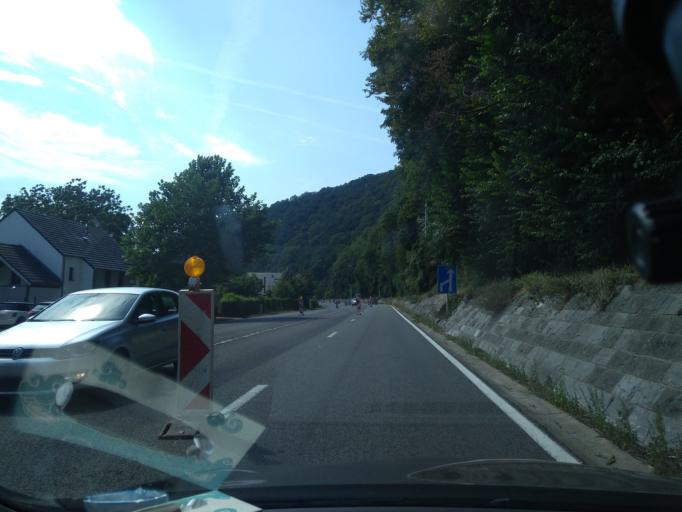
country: BE
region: Wallonia
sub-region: Province de Namur
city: Profondeville
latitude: 50.3520
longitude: 4.8597
